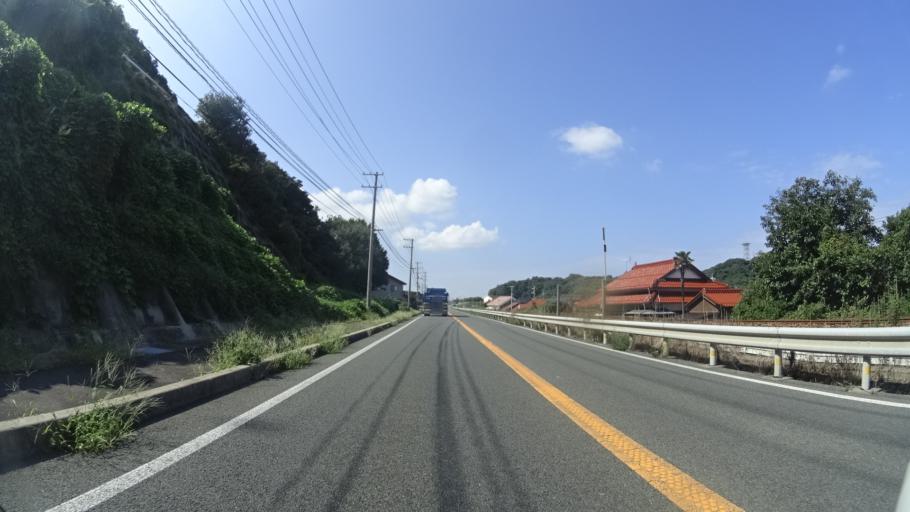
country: JP
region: Shimane
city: Gotsucho
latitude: 35.0327
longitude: 132.2424
